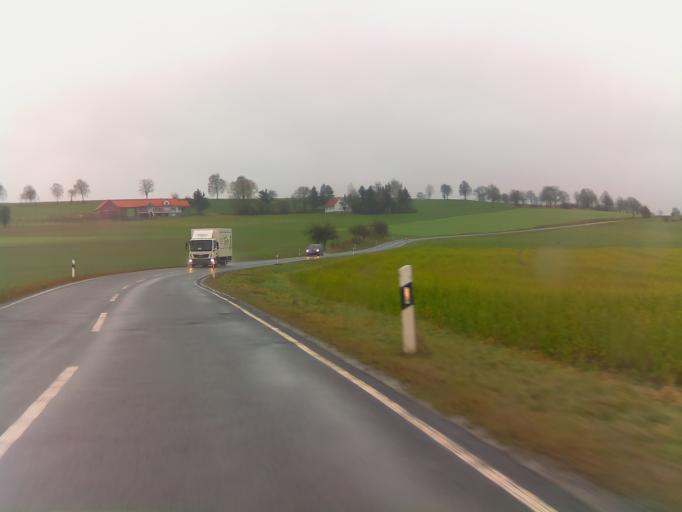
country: DE
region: Hesse
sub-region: Regierungsbezirk Kassel
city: Dipperz
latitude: 50.4837
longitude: 9.7799
